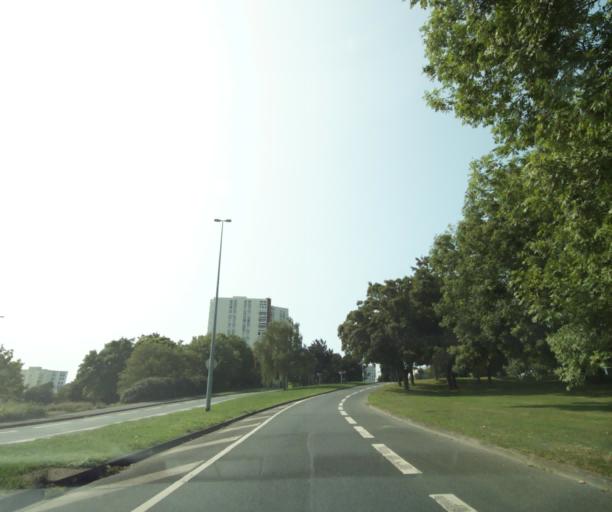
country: FR
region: Lower Normandy
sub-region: Departement du Calvados
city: Caen
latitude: 49.1985
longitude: -0.3442
